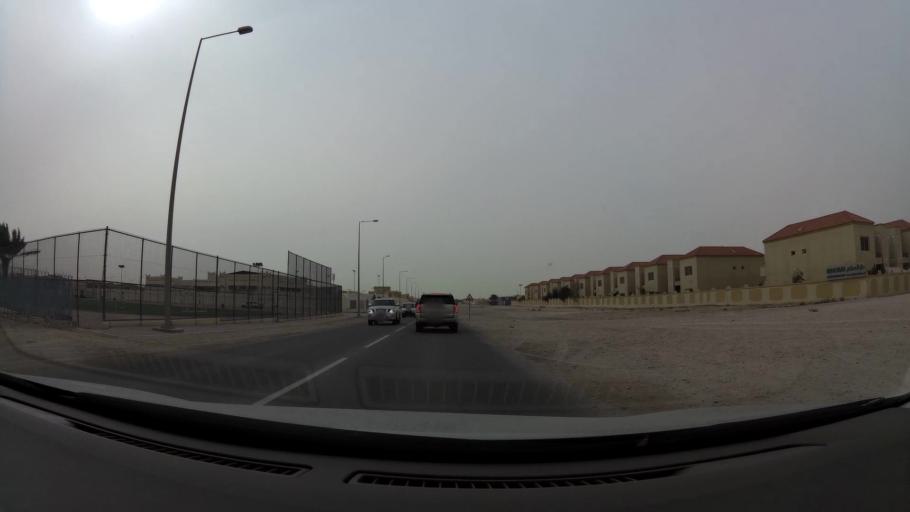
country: QA
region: Baladiyat ad Dawhah
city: Doha
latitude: 25.2423
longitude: 51.5120
